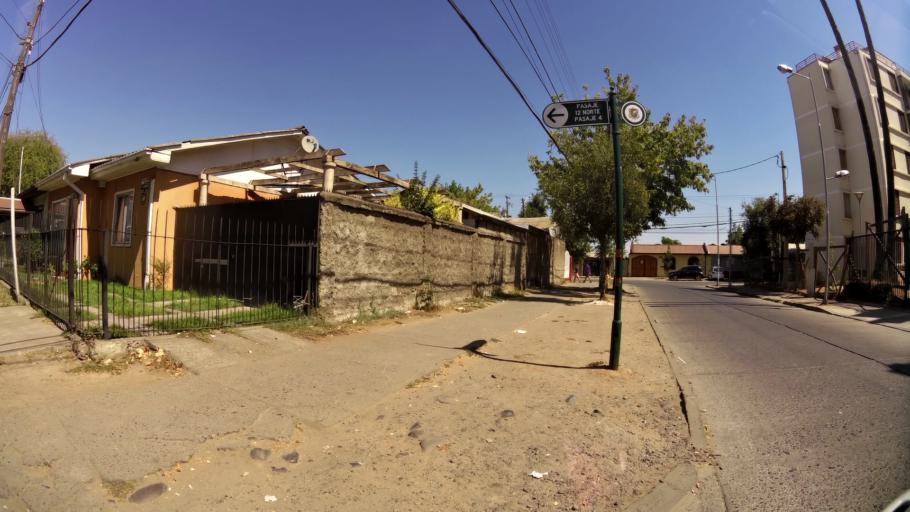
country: CL
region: Maule
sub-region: Provincia de Talca
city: Talca
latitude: -35.4138
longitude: -71.6520
